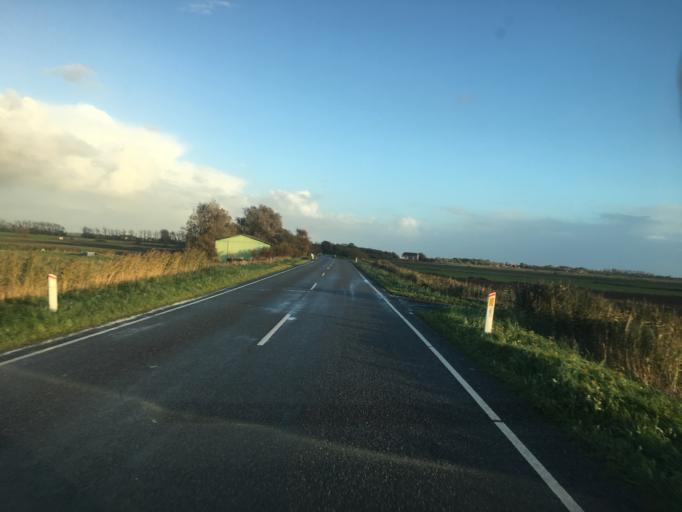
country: DE
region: Schleswig-Holstein
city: Rodenas
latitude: 54.9167
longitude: 8.7331
